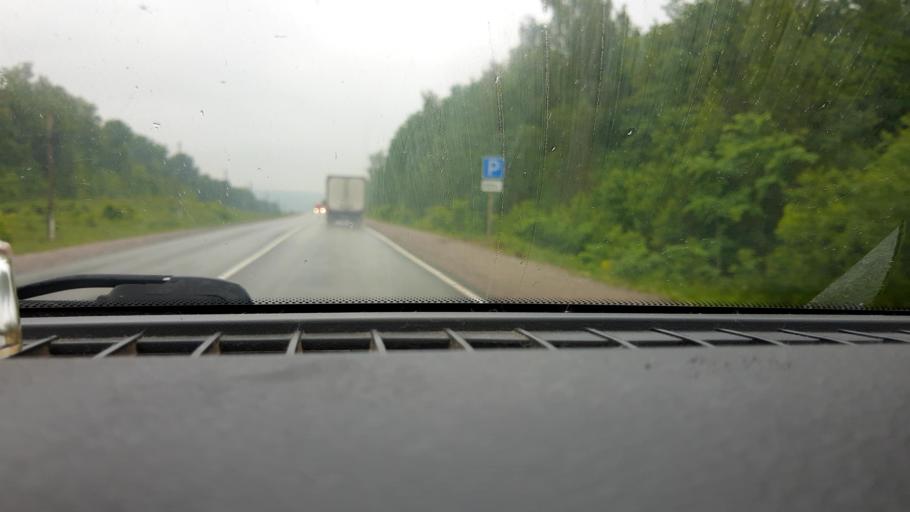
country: RU
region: Bashkortostan
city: Belebey
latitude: 54.2202
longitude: 54.0751
